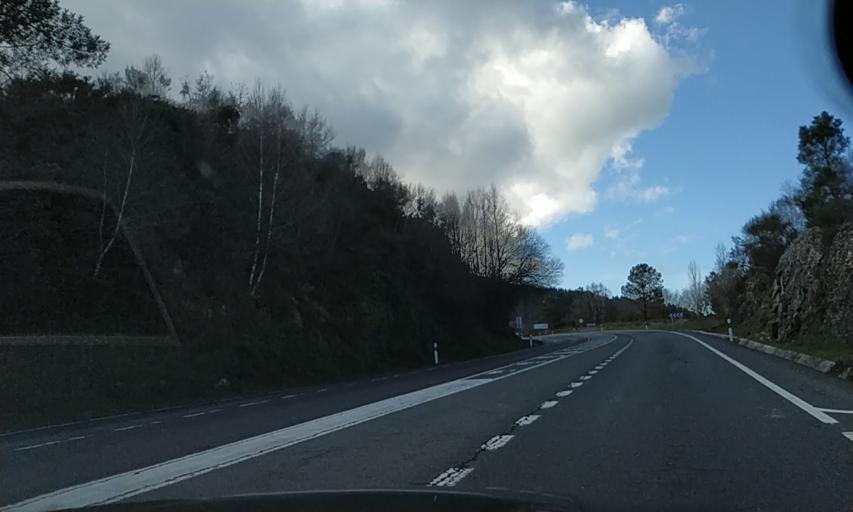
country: ES
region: Galicia
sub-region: Provincia de Pontevedra
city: Silleda
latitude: 42.6980
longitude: -8.3321
